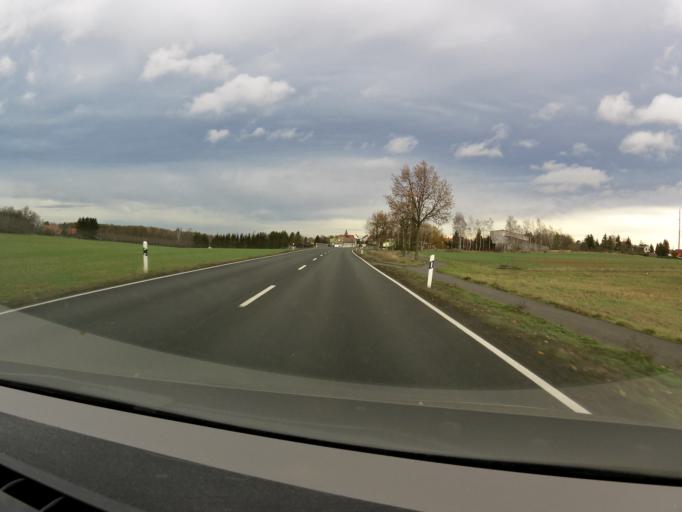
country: DE
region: Saxony-Anhalt
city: Blankenheim
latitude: 51.5595
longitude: 11.4202
